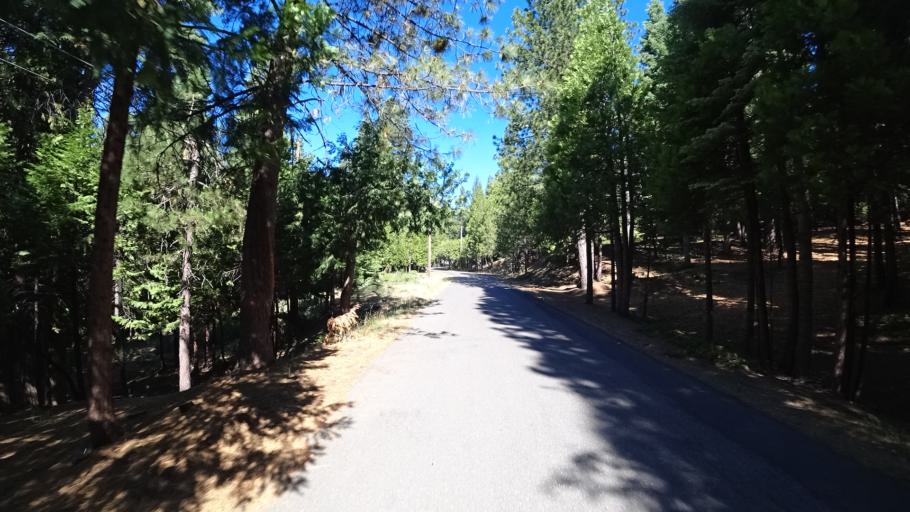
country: US
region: California
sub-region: Calaveras County
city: Arnold
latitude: 38.2928
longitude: -120.2689
